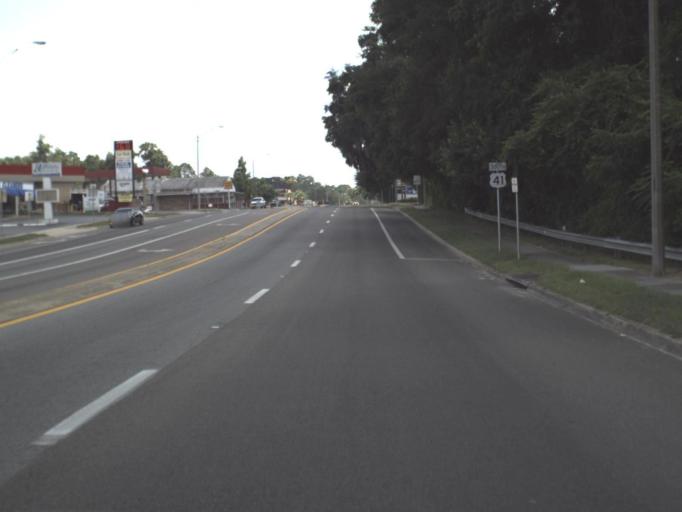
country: US
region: Florida
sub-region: Columbia County
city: Lake City
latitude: 30.1831
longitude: -82.6394
